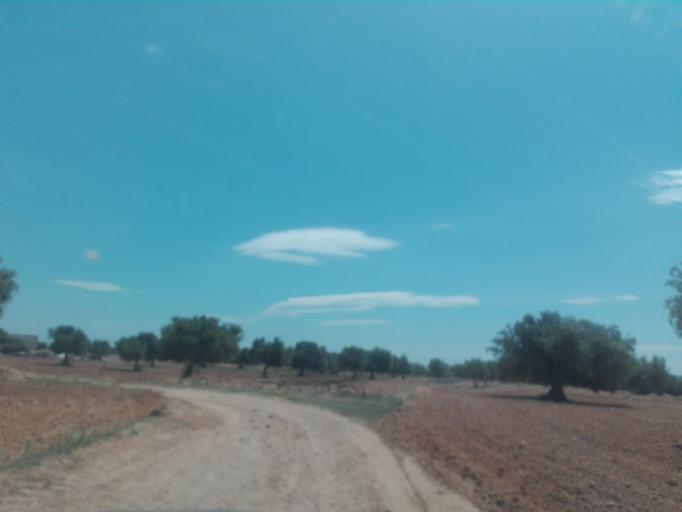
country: TN
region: Safaqis
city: Sfax
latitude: 34.6537
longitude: 10.5920
